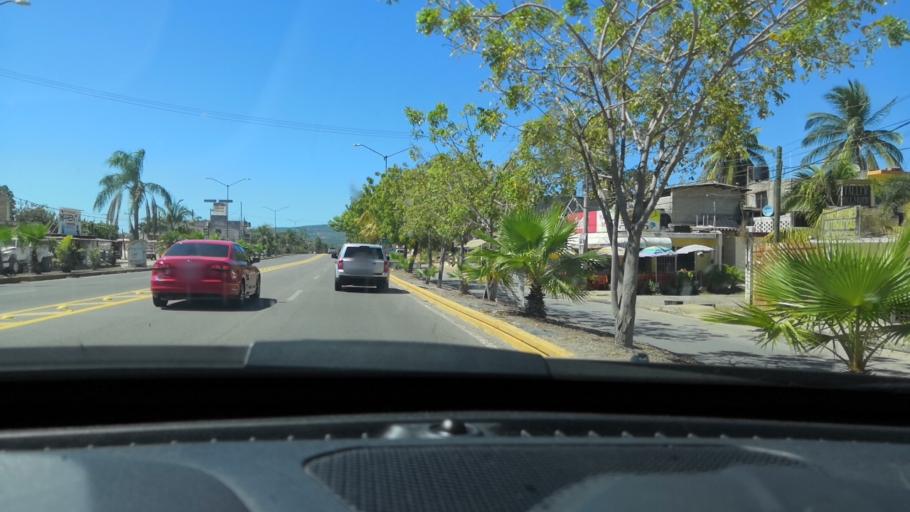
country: MX
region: Nayarit
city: Las Varas
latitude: 21.1826
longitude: -105.1314
